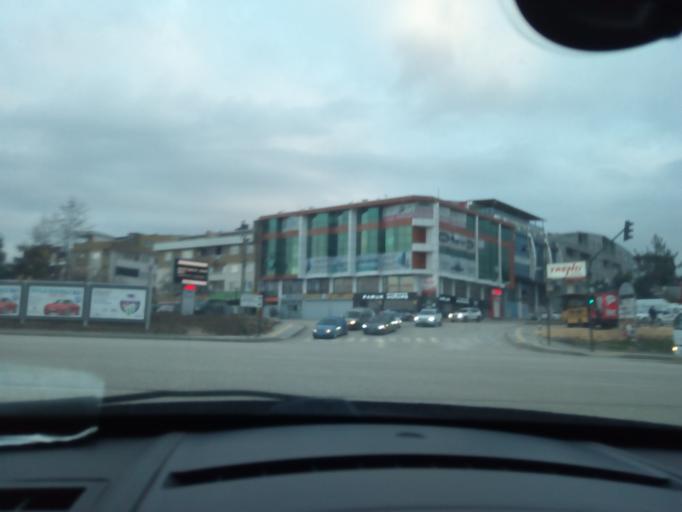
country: TR
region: Bursa
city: Niluefer
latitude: 40.2336
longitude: 28.9692
